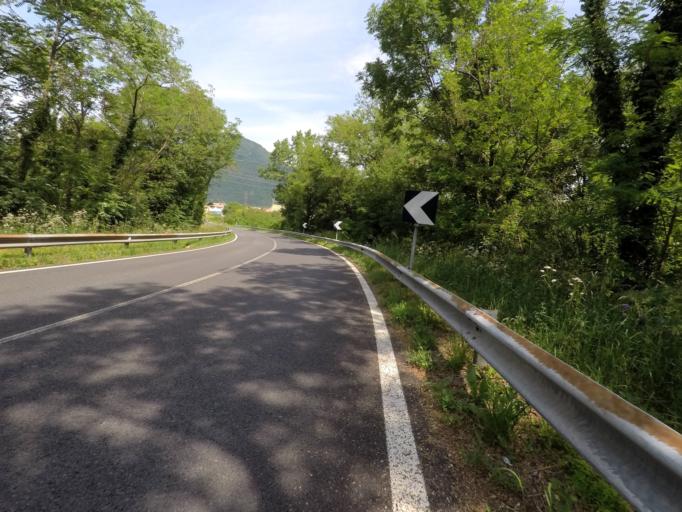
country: IT
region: Friuli Venezia Giulia
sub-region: Provincia di Udine
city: Tolmezzo
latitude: 46.3932
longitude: 13.0146
